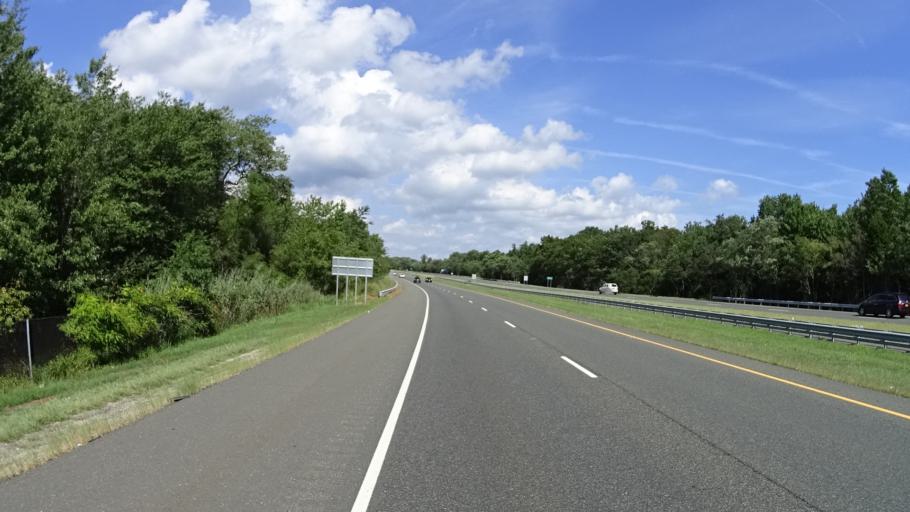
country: US
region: New Jersey
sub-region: Monmouth County
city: Eatontown
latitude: 40.2696
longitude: -74.0624
